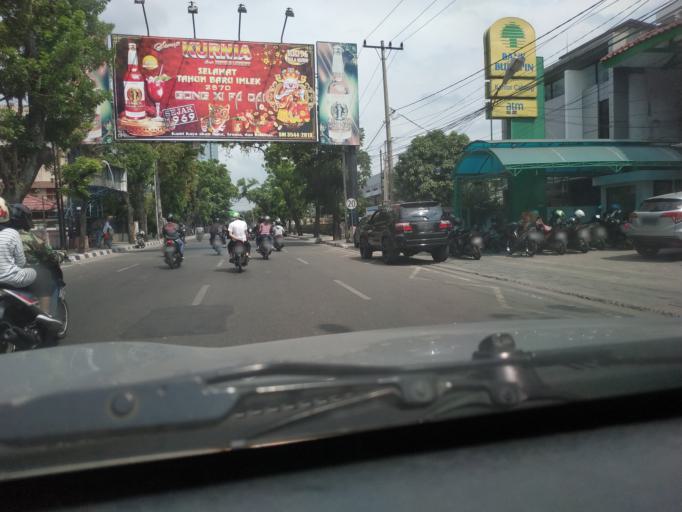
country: ID
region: North Sumatra
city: Medan
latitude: 3.5845
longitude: 98.6628
